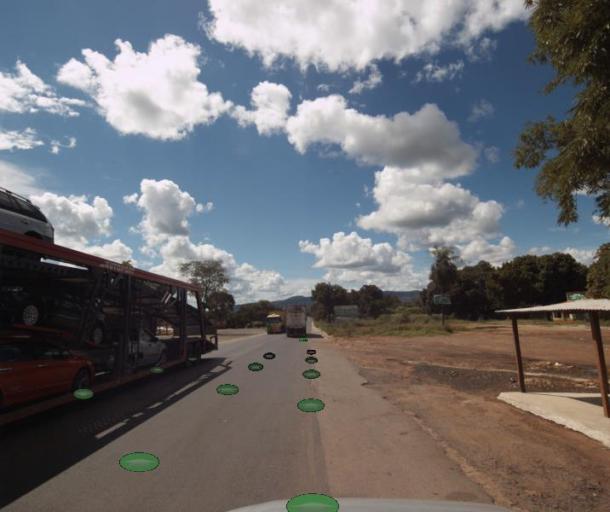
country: BR
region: Goias
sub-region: Porangatu
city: Porangatu
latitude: -13.7120
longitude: -49.0210
